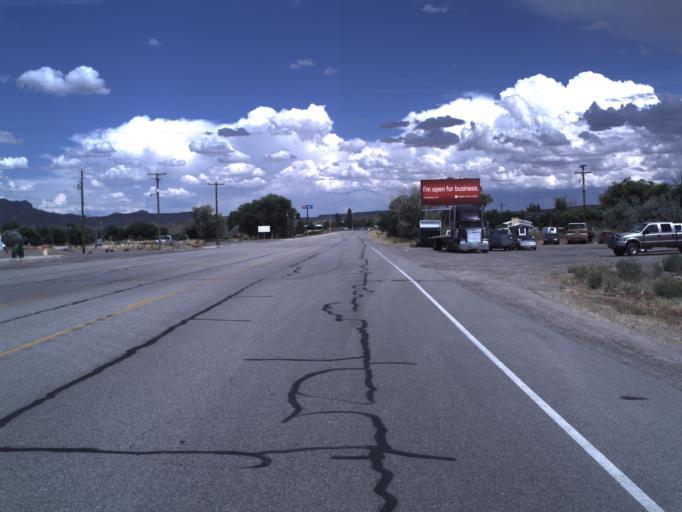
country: US
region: Utah
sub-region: Carbon County
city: East Carbon City
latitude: 38.9949
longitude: -110.1497
